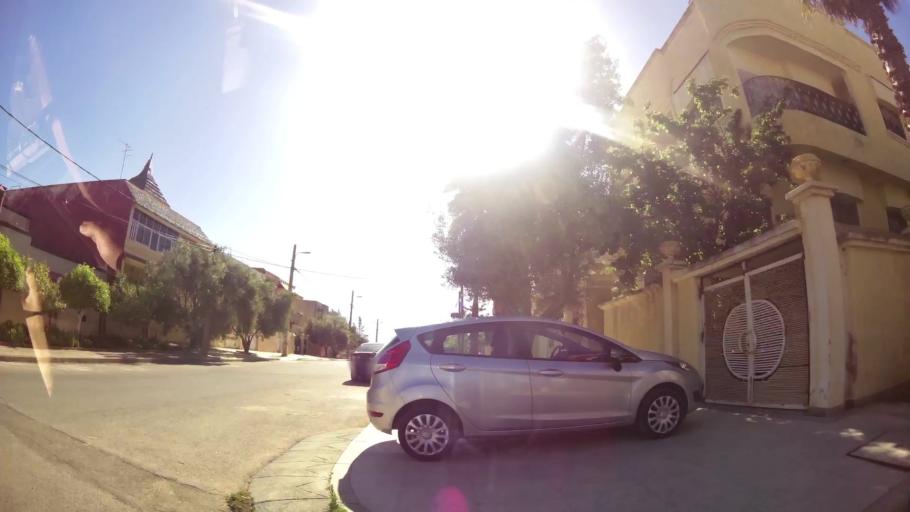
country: MA
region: Oriental
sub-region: Oujda-Angad
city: Oujda
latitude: 34.6492
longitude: -1.8926
